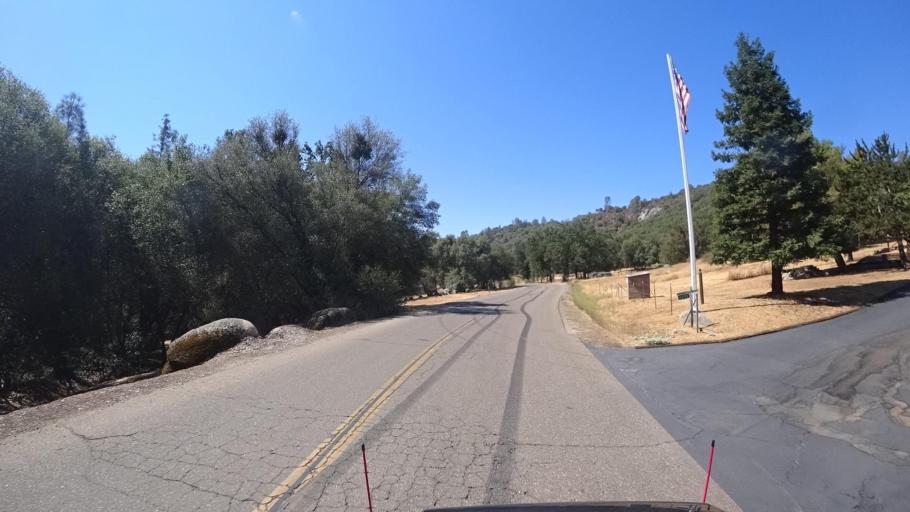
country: US
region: California
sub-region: Mariposa County
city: Mariposa
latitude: 37.4386
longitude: -119.9077
